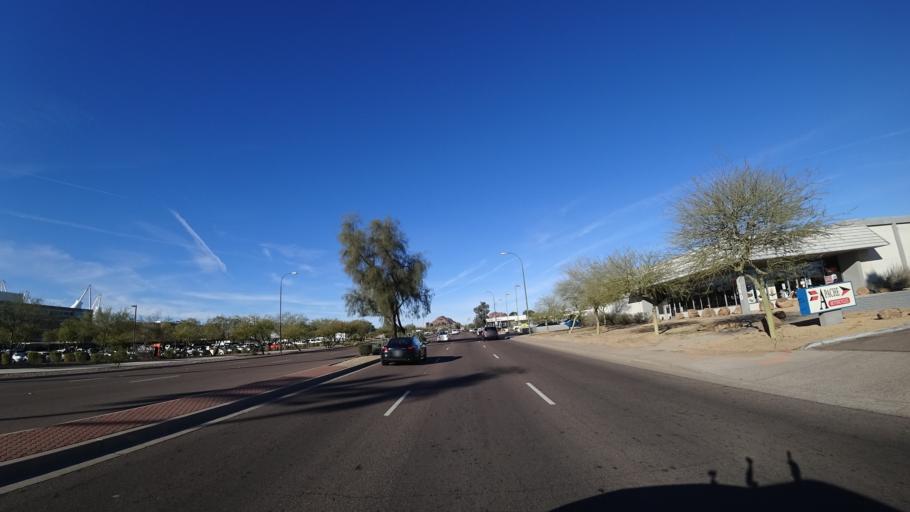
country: US
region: Arizona
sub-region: Maricopa County
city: Scottsdale
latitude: 33.4658
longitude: -111.9224
